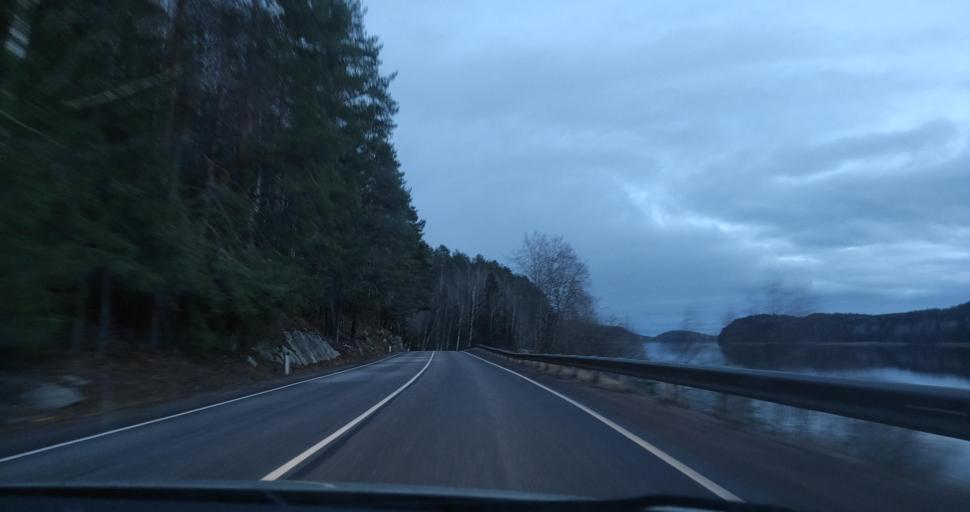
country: RU
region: Republic of Karelia
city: Sortavala
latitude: 61.7832
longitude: 30.7695
